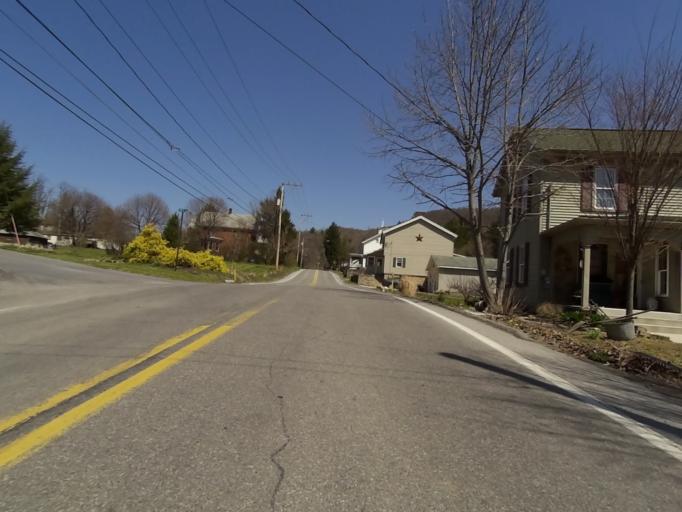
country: US
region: Pennsylvania
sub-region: Blair County
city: Tyrone
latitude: 40.6098
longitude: -78.1340
